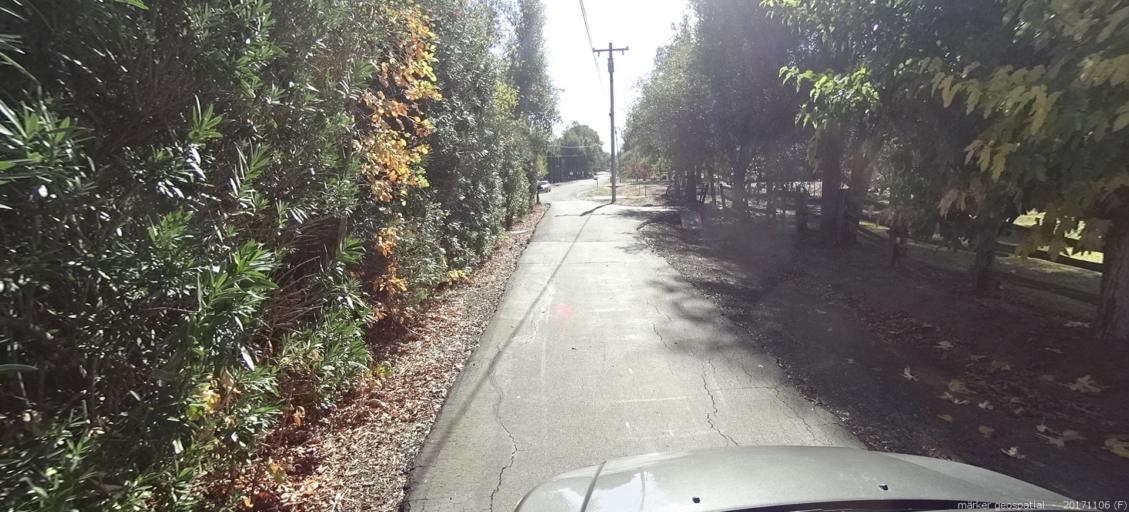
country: US
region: California
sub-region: Shasta County
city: Palo Cedro
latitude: 40.5786
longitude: -122.2244
